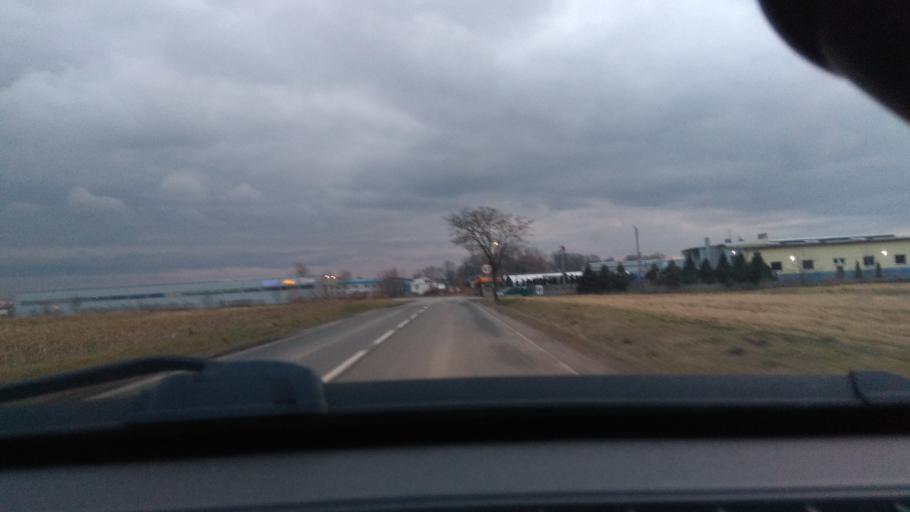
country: PL
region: Greater Poland Voivodeship
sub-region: Powiat kepinski
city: Kepno
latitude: 51.2898
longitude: 18.0061
